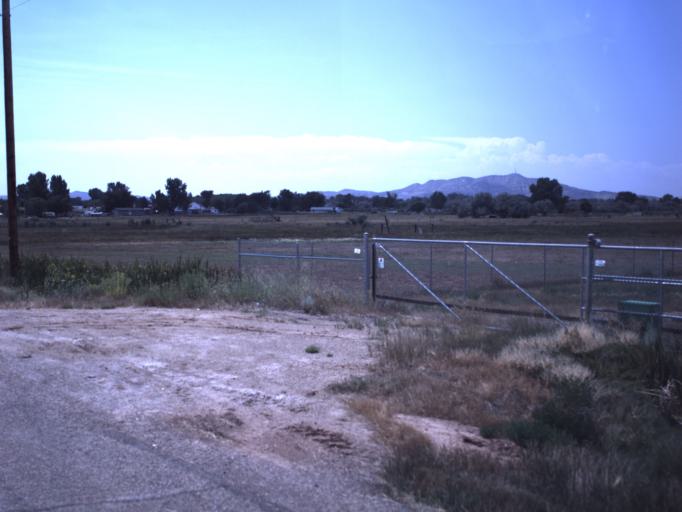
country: US
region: Utah
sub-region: Uintah County
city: Vernal
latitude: 40.4972
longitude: -109.5292
